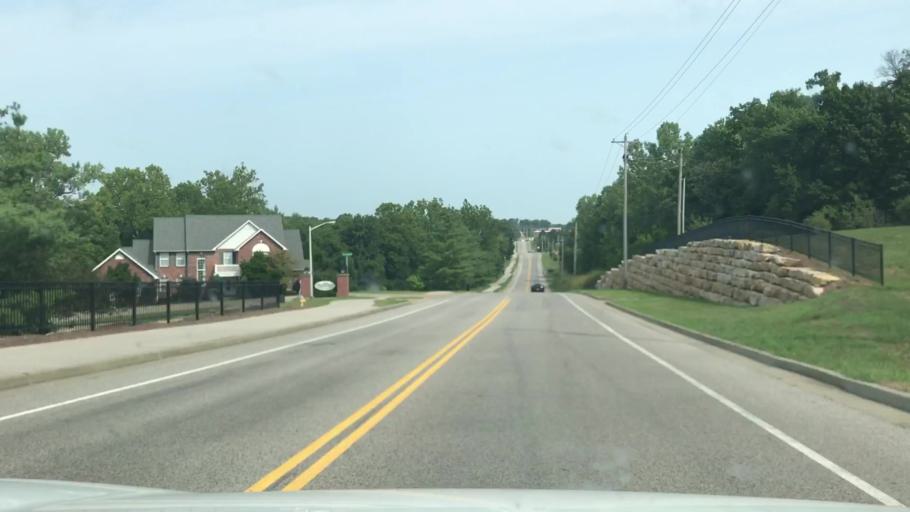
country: US
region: Missouri
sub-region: Saint Charles County
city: Cottleville
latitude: 38.7188
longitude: -90.6420
